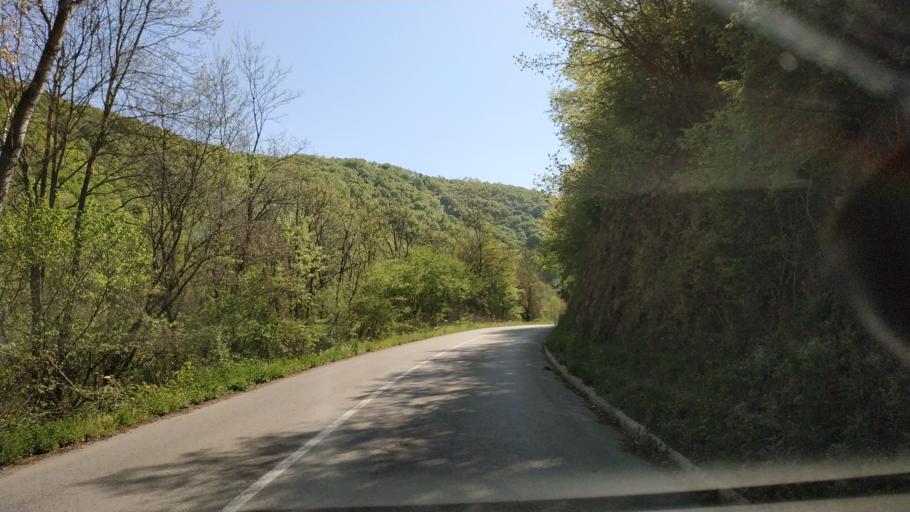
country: RS
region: Central Serbia
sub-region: Nisavski Okrug
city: Nis
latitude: 43.4194
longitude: 21.8487
